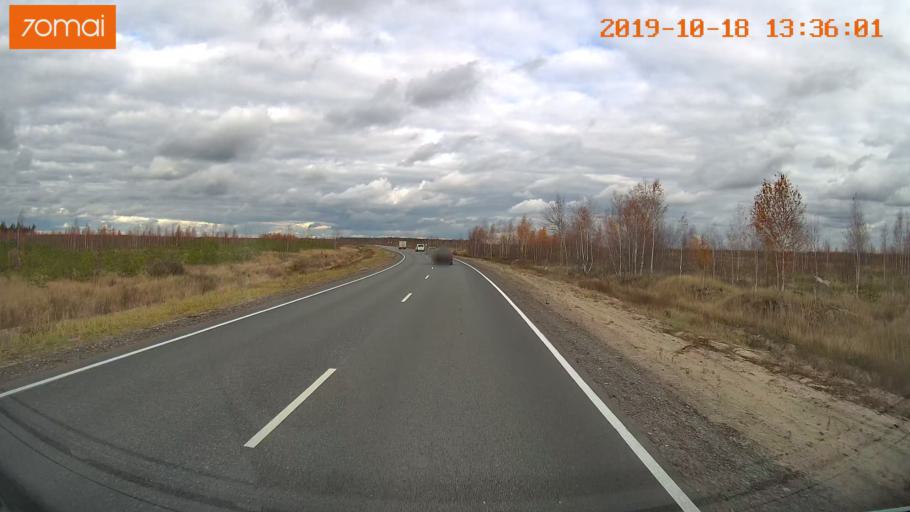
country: RU
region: Rjazan
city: Solotcha
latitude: 54.8658
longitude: 39.9795
